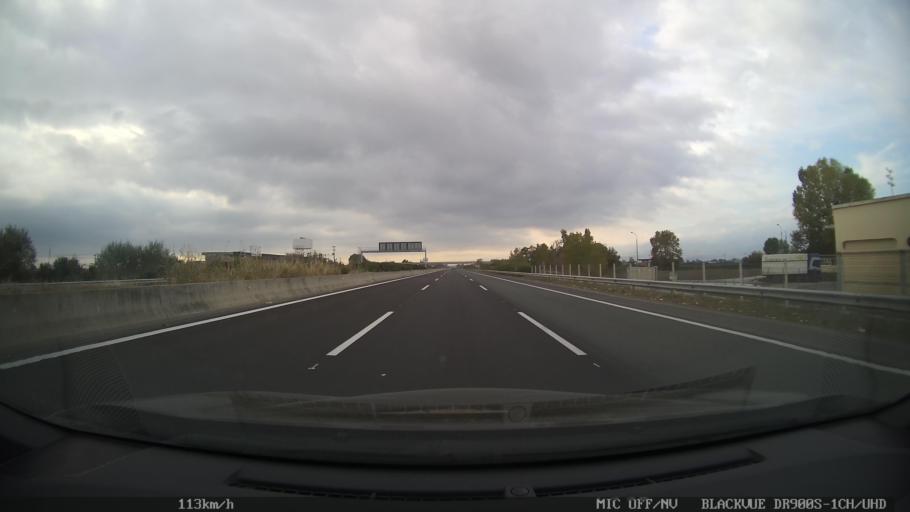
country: GR
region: Central Macedonia
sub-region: Nomos Pierias
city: Peristasi
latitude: 40.2473
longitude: 22.5340
